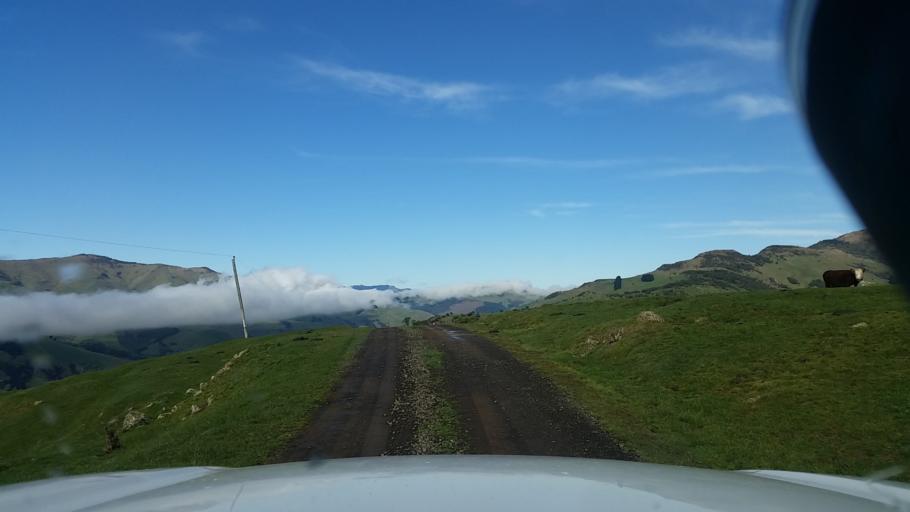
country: NZ
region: Canterbury
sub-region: Christchurch City
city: Christchurch
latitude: -43.6653
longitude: 172.8755
